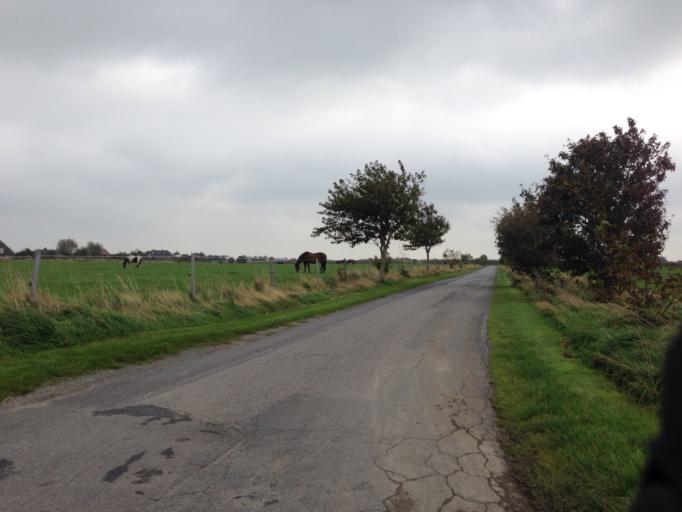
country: DE
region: Schleswig-Holstein
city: Alkersum
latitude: 54.7042
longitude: 8.5071
